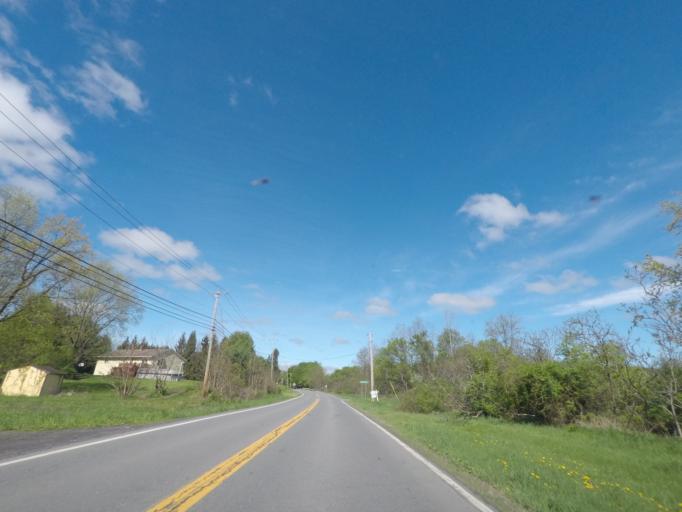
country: US
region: New York
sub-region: Albany County
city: Ravena
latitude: 42.4676
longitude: -73.8674
